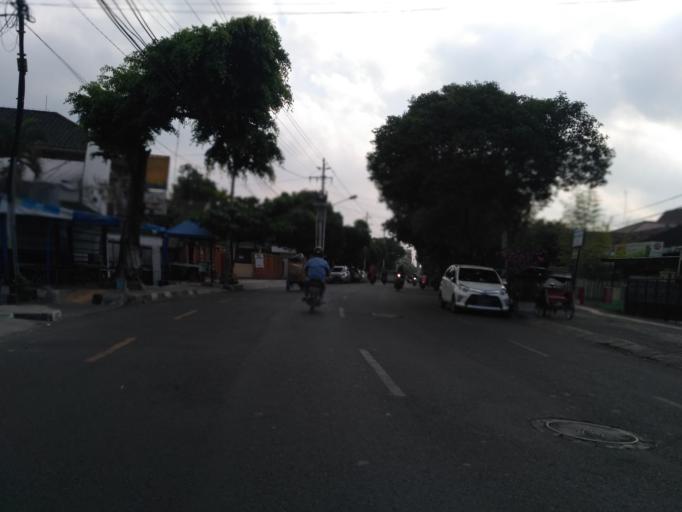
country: ID
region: Daerah Istimewa Yogyakarta
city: Yogyakarta
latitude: -7.7949
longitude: 110.3726
